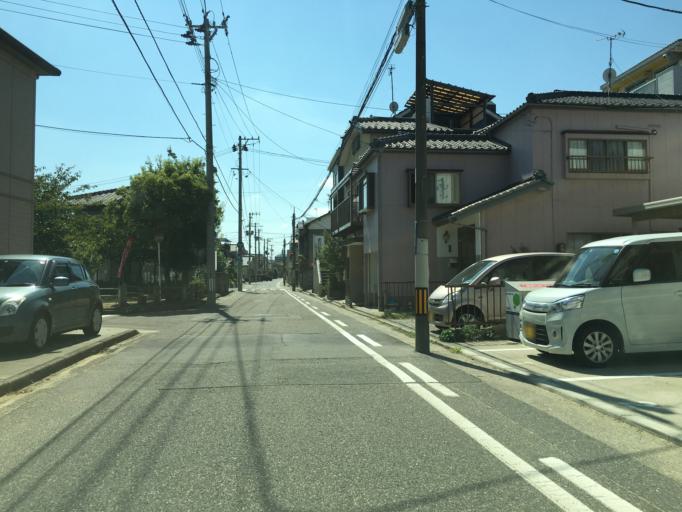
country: JP
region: Niigata
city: Niigata-shi
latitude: 37.9061
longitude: 139.0165
